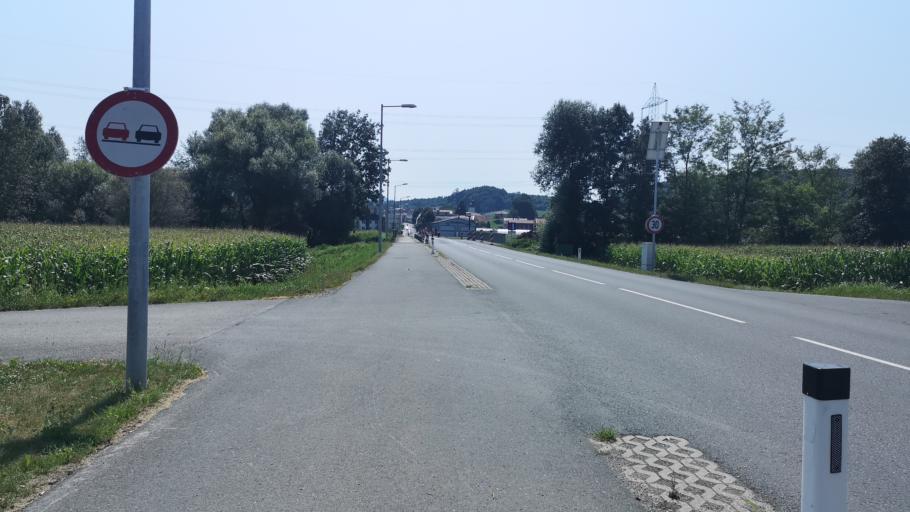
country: AT
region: Styria
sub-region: Politischer Bezirk Deutschlandsberg
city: Wettmannstatten
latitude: 46.8356
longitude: 15.3816
